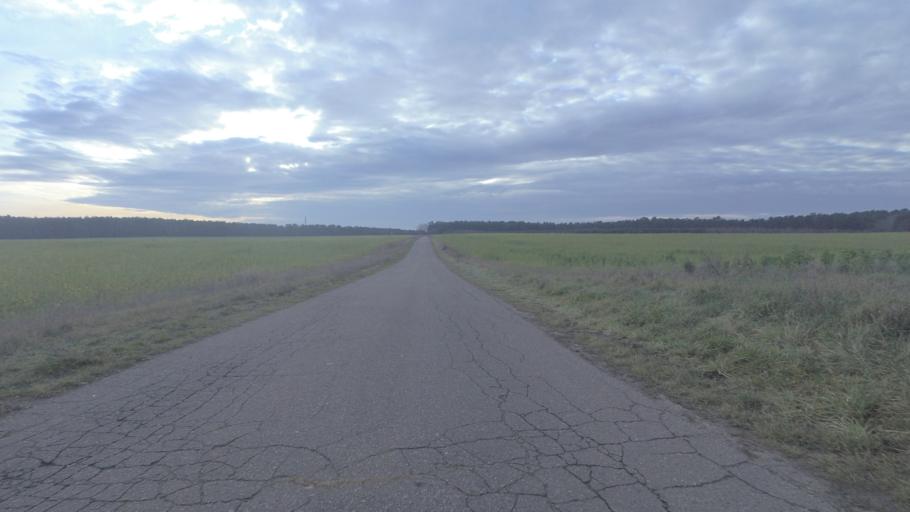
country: DE
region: Brandenburg
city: Am Mellensee
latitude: 52.2367
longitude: 13.3633
